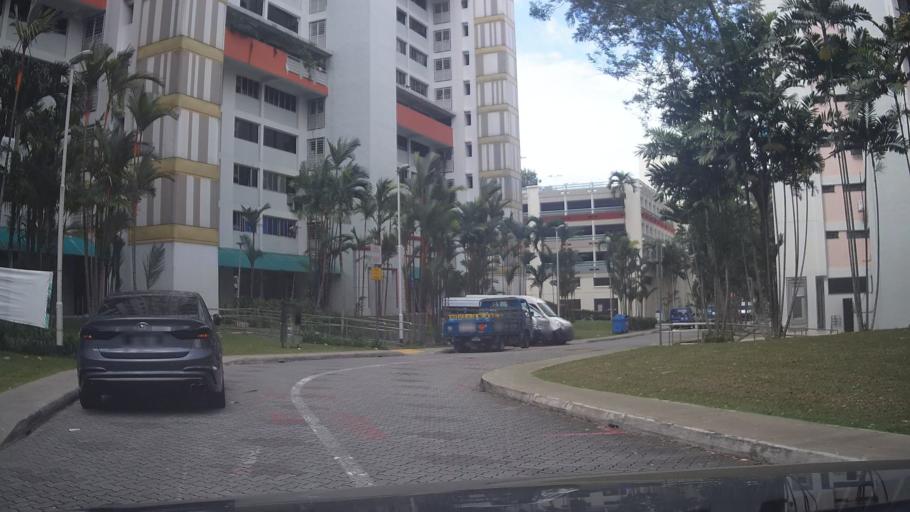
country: MY
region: Johor
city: Johor Bahru
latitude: 1.4420
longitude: 103.7768
